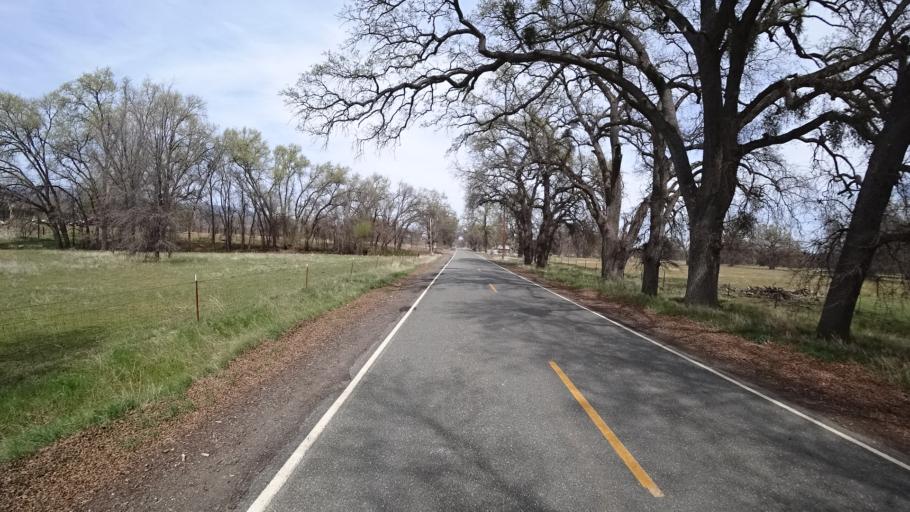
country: US
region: California
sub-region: Colusa County
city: Maxwell
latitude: 39.3937
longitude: -122.5519
